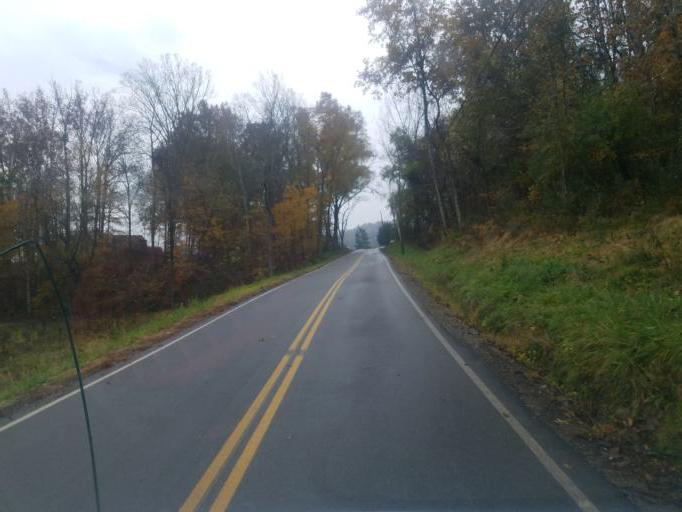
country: US
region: Ohio
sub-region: Morgan County
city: McConnelsville
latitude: 39.5542
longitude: -81.7975
